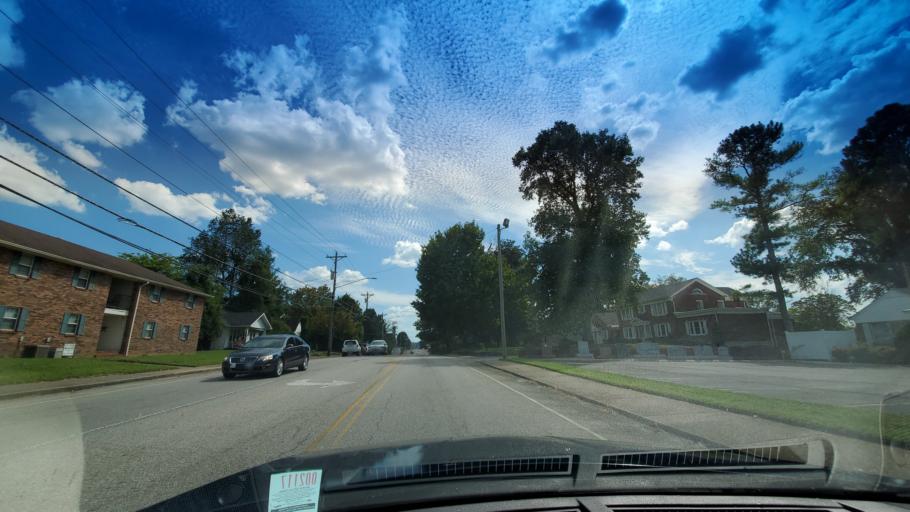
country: US
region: Tennessee
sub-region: Smith County
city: Carthage
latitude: 36.2580
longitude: -85.9512
